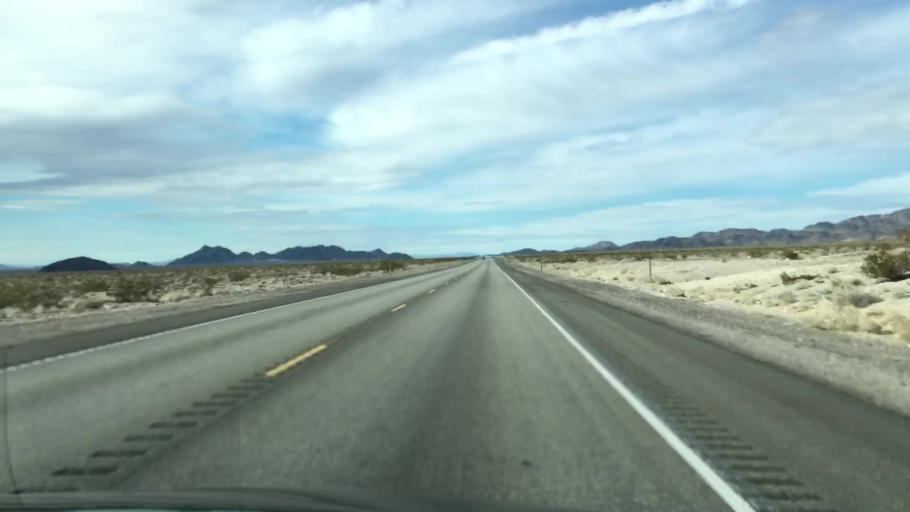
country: US
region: Nevada
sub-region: Nye County
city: Pahrump
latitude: 36.5898
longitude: -116.2230
